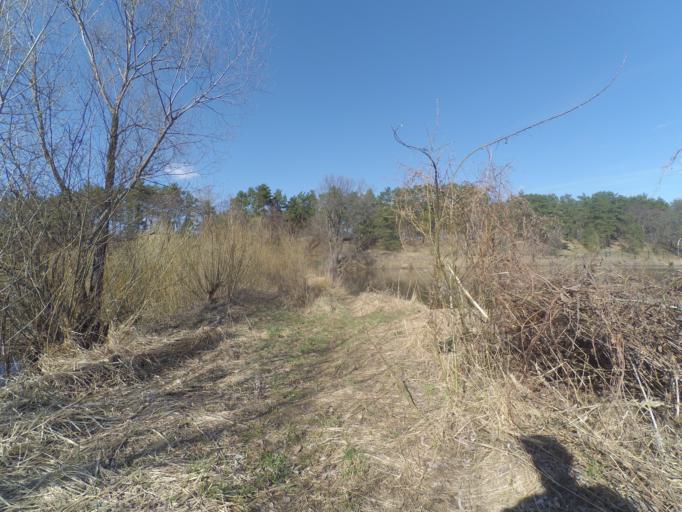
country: RU
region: Moskovskaya
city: Stupino
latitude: 54.8401
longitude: 38.0690
